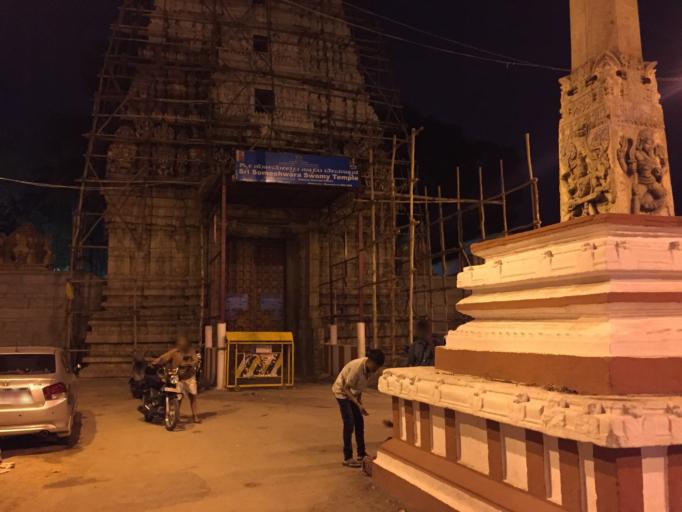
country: IN
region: Karnataka
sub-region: Bangalore Urban
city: Bangalore
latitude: 12.9755
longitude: 77.6245
